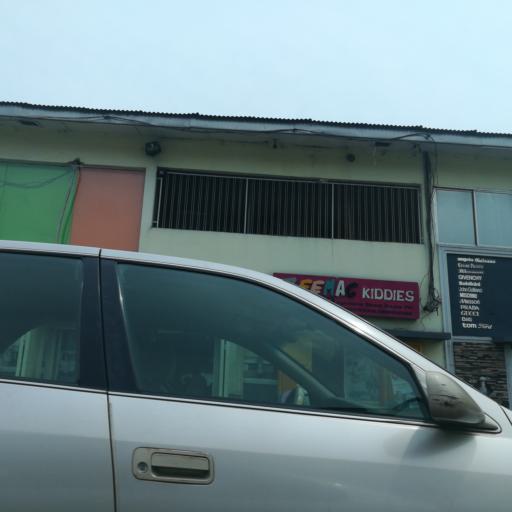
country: NG
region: Rivers
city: Port Harcourt
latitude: 4.8033
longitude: 7.0063
